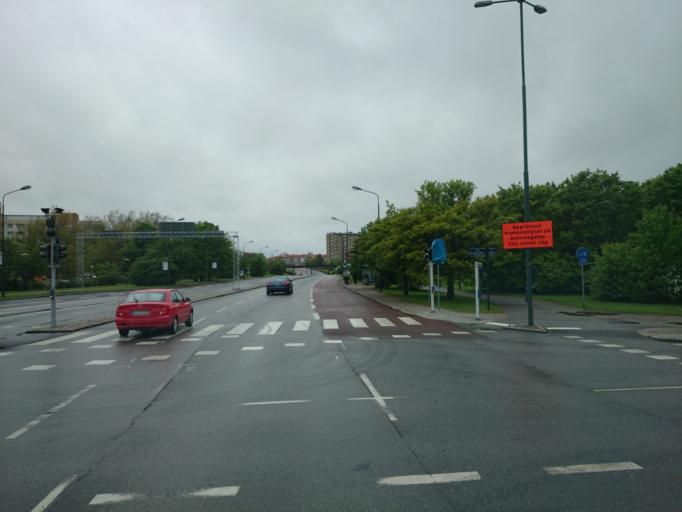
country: SE
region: Skane
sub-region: Malmo
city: Malmoe
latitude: 55.5888
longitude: 13.0366
